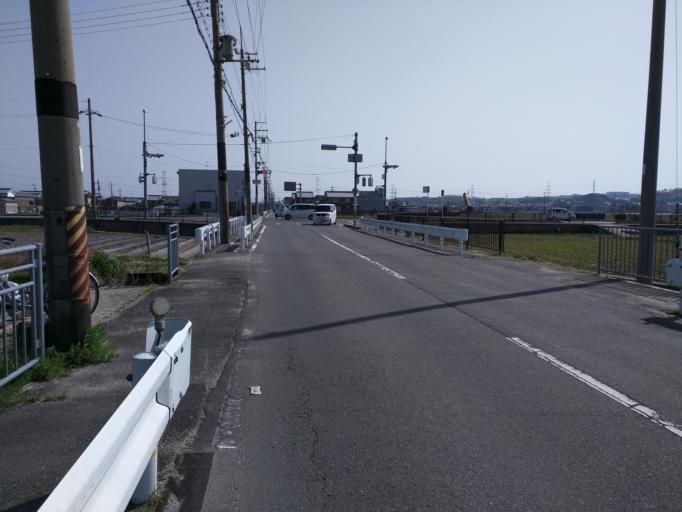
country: JP
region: Kyoto
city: Tanabe
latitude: 34.7692
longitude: 135.7975
